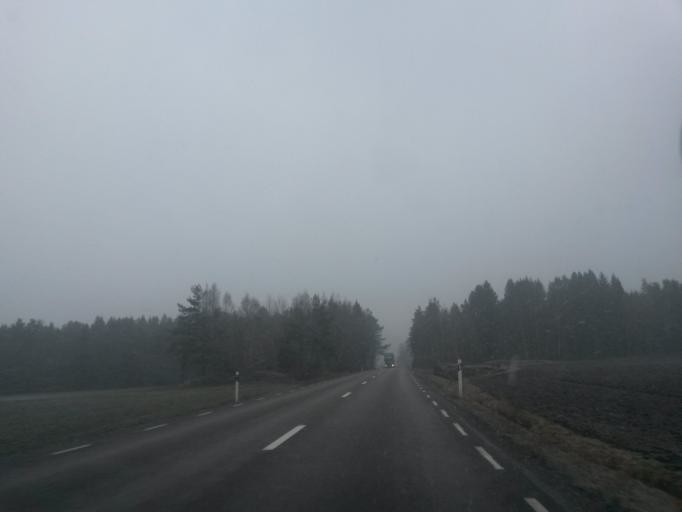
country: SE
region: Vaestra Goetaland
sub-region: Vanersborgs Kommun
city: Vargon
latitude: 58.2236
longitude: 12.4235
